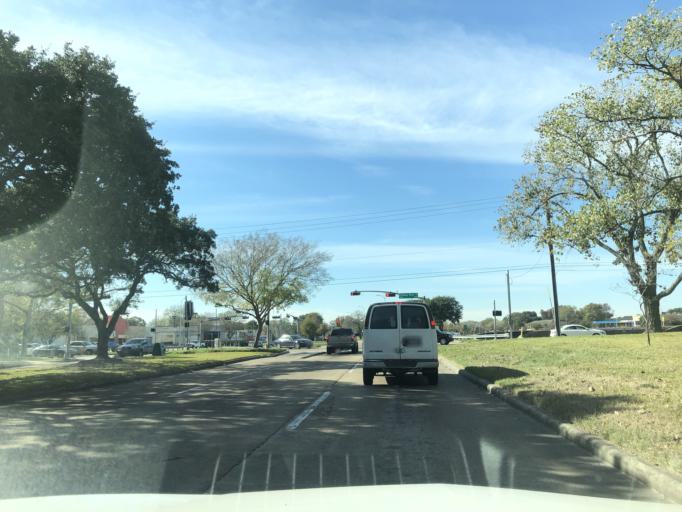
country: US
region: Texas
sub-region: Harris County
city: Bellaire
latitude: 29.6771
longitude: -95.4759
